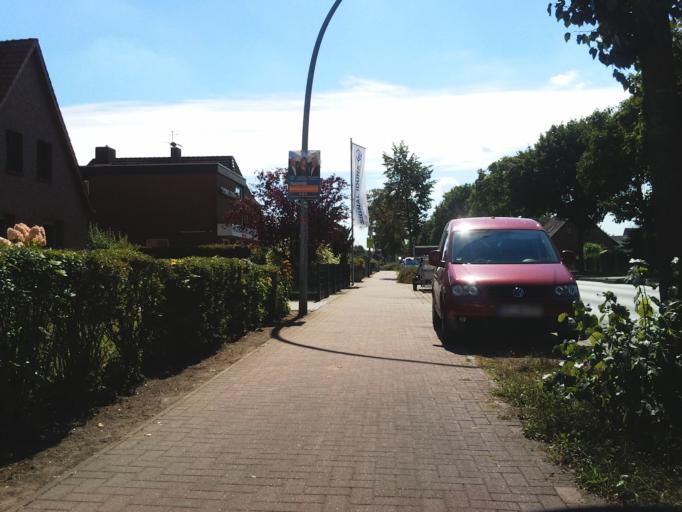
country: DE
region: Lower Saxony
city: Nienburg
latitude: 52.6662
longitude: 9.2233
